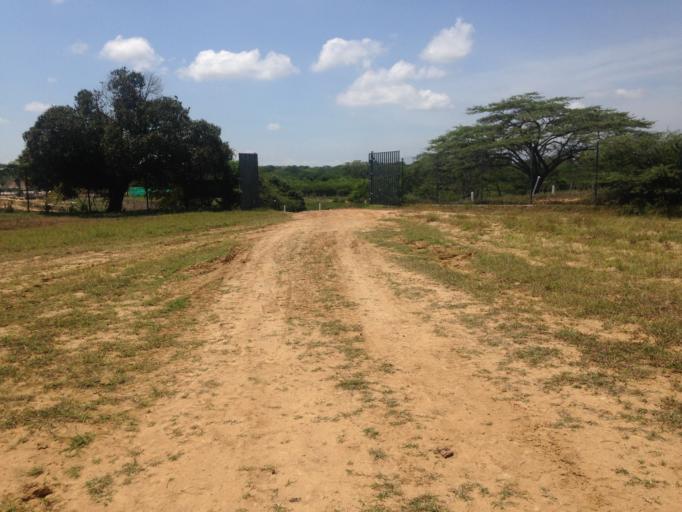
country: CO
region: Atlantico
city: Baranoa
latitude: 10.8417
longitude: -74.9046
